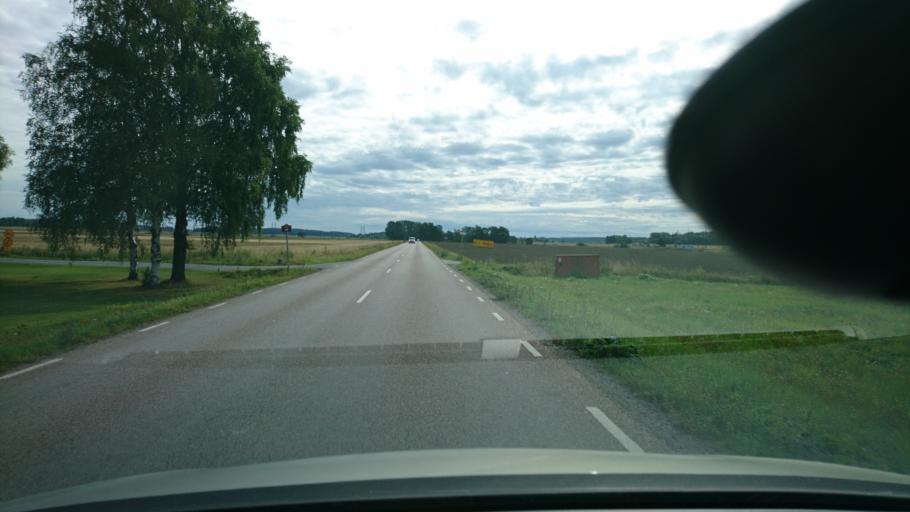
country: SE
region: Uppsala
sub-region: Uppsala Kommun
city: Saevja
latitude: 59.8319
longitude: 17.6985
